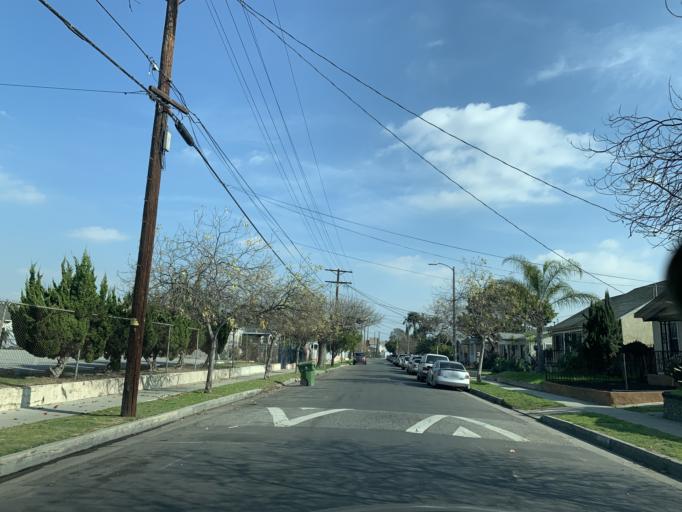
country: US
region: California
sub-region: Los Angeles County
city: Willowbrook
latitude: 33.9302
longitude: -118.2428
